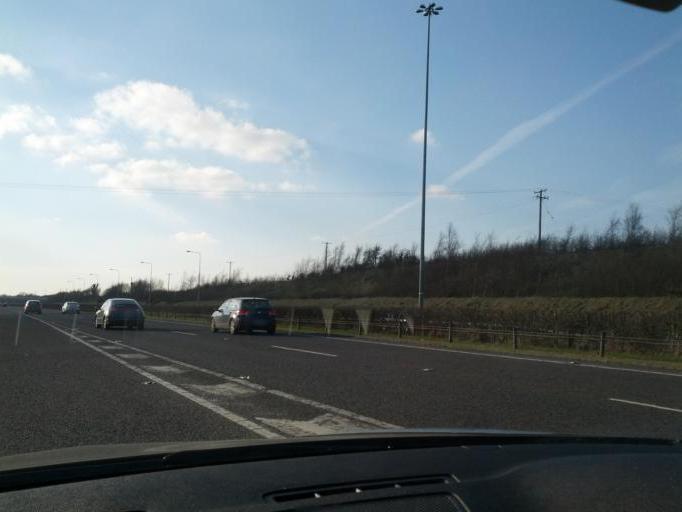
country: IE
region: Leinster
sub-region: Kildare
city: Kildare
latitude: 53.1527
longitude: -6.9255
